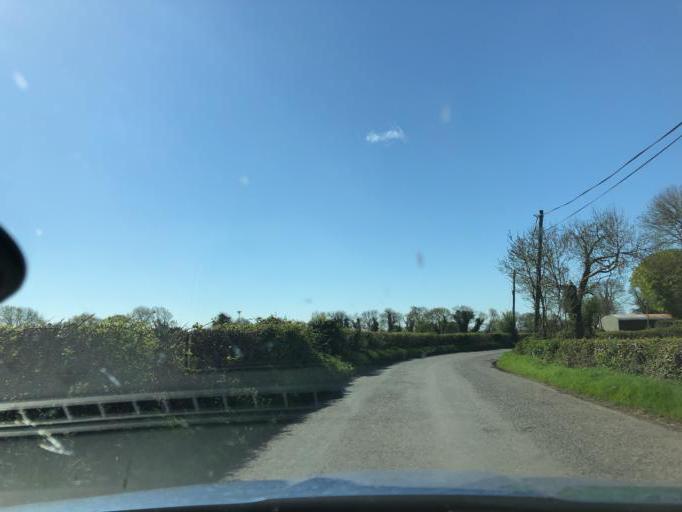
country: IE
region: Connaught
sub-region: County Galway
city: Portumna
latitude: 53.1803
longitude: -8.1765
